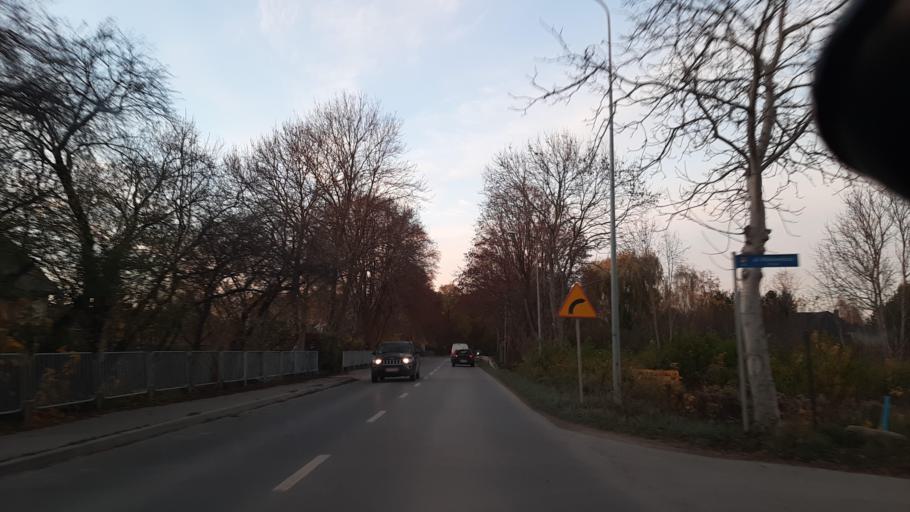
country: PL
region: Lublin Voivodeship
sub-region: Powiat lubelski
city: Jastkow
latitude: 51.2890
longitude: 22.4969
